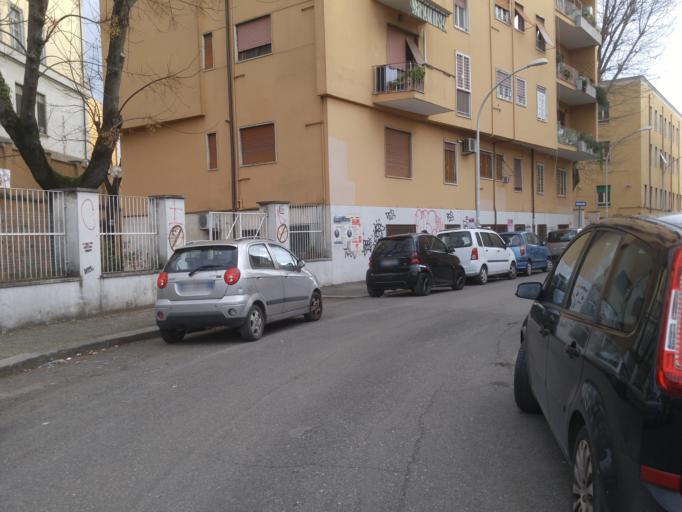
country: IT
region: Latium
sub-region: Citta metropolitana di Roma Capitale
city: Rome
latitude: 41.8617
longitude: 12.4873
